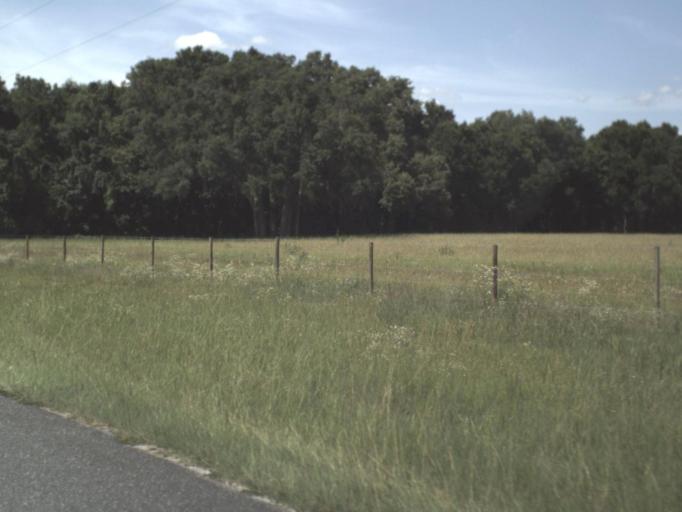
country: US
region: Florida
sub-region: Alachua County
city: High Springs
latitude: 29.8511
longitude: -82.7419
